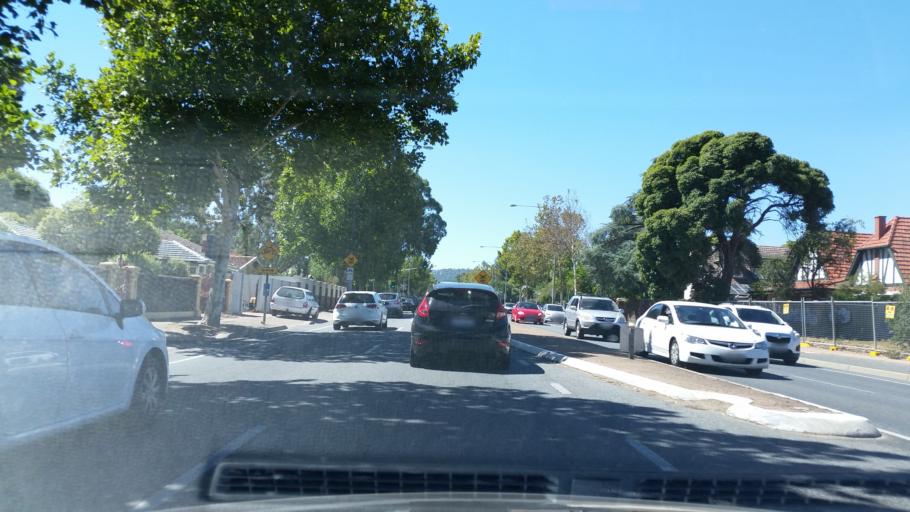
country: AU
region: South Australia
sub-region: Unley
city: Unley Park
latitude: -34.9661
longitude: 138.5957
